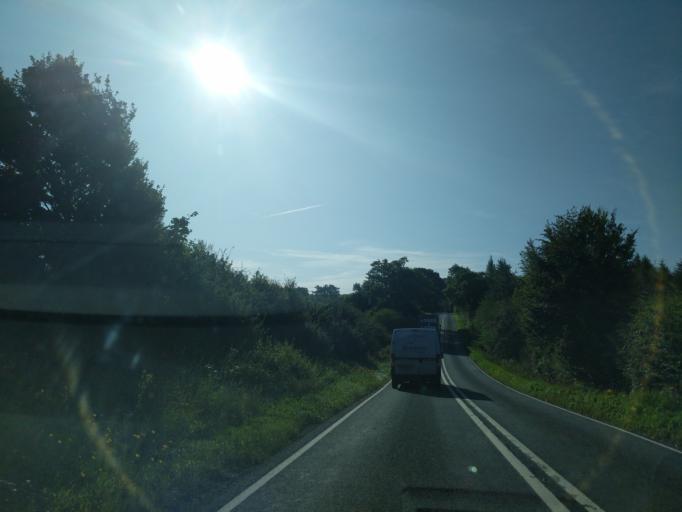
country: GB
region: England
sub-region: Lincolnshire
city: Bourne
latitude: 52.8015
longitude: -0.4741
